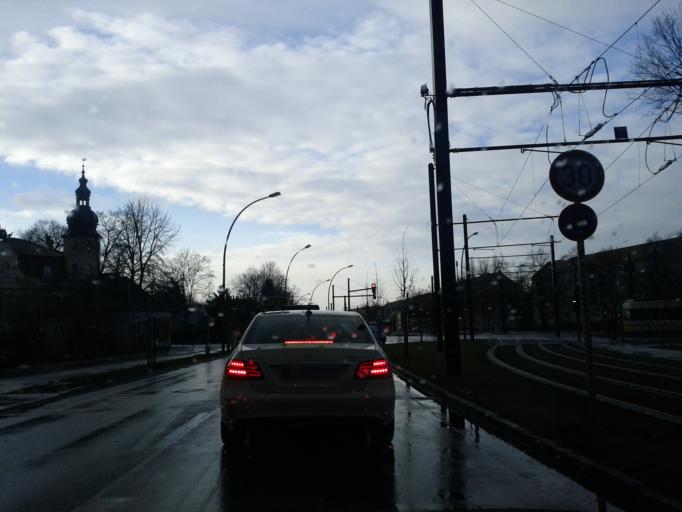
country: DE
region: Berlin
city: Berlin Koepenick
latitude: 52.4513
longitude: 13.6019
